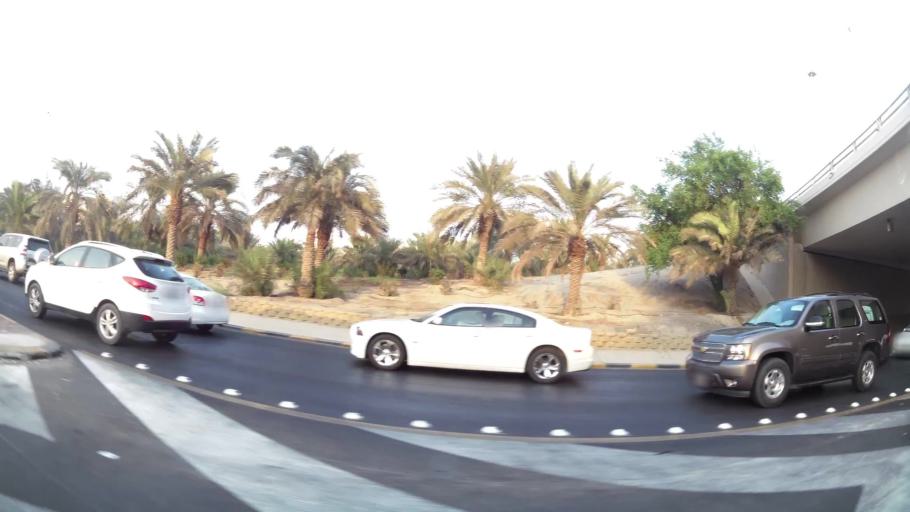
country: KW
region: Muhafazat Hawalli
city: Hawalli
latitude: 29.3312
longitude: 48.0397
